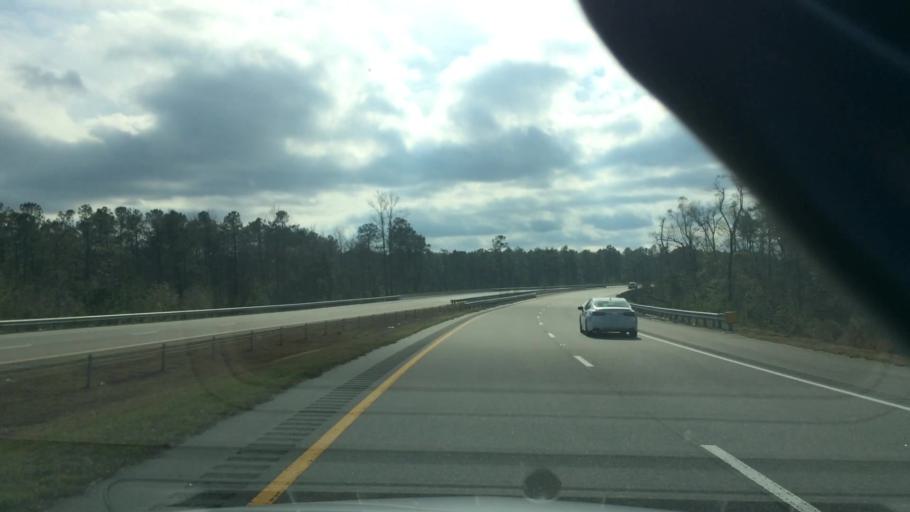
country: US
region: North Carolina
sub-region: Brunswick County
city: Leland
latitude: 34.2094
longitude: -78.0768
